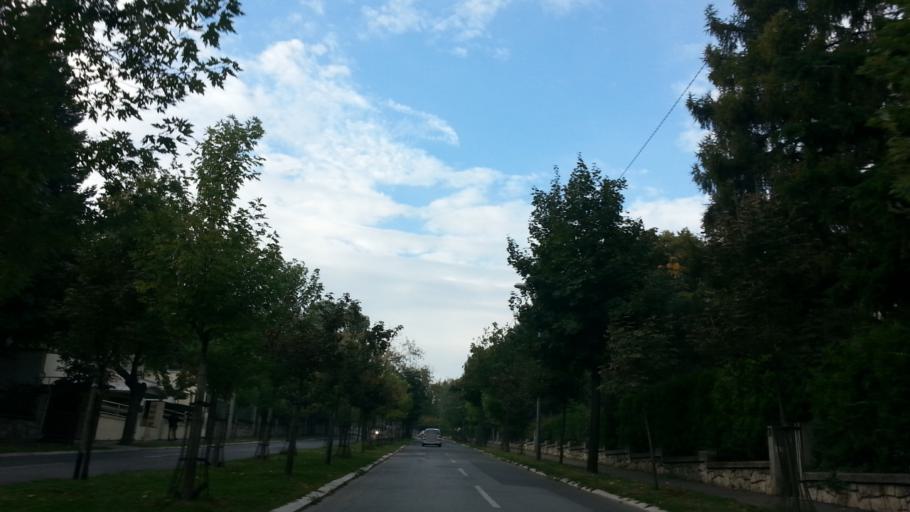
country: RS
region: Central Serbia
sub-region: Belgrade
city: Savski Venac
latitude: 44.7745
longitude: 20.4561
